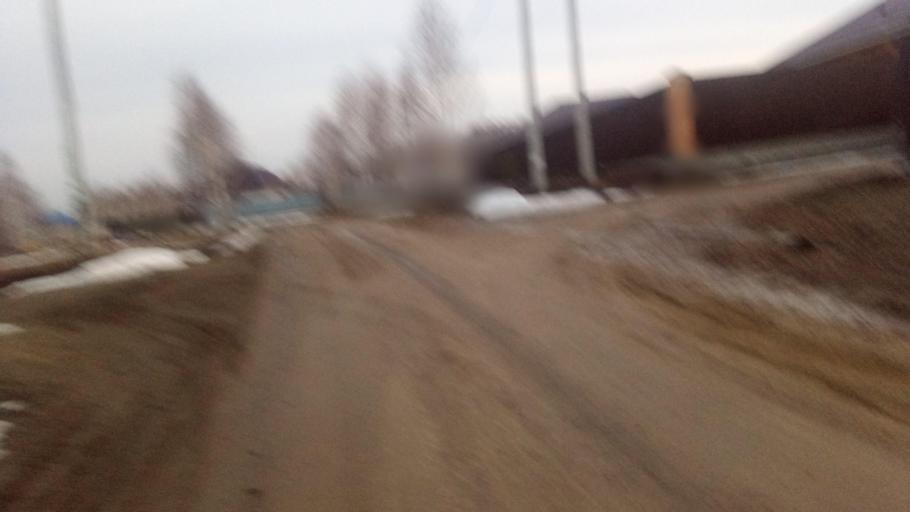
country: RU
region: Chelyabinsk
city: Sargazy
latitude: 55.1030
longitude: 61.2017
